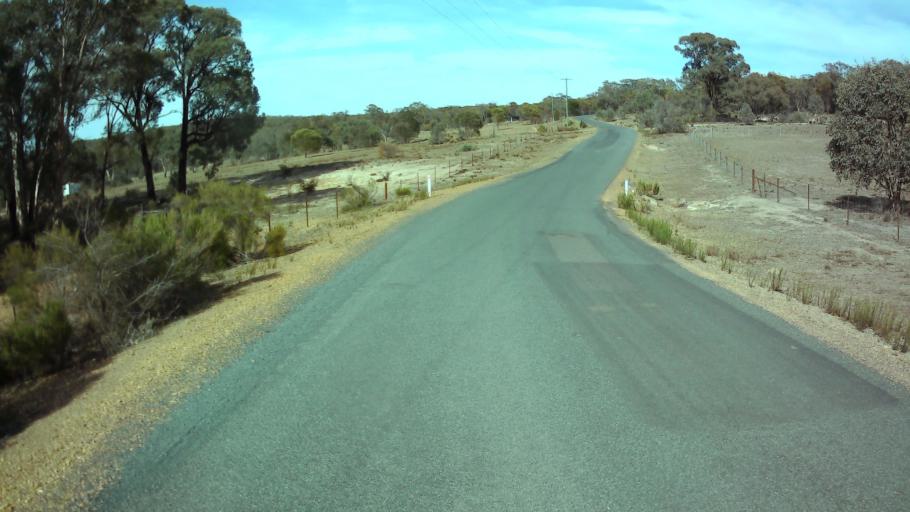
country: AU
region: New South Wales
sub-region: Weddin
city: Grenfell
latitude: -33.8786
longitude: 148.1977
